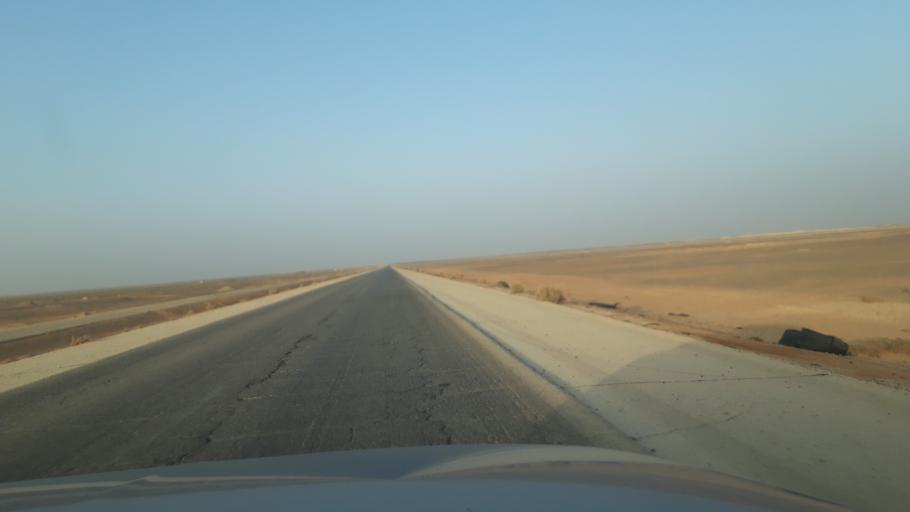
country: JO
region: Ma'an
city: Al Jafr
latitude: 30.2101
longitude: 36.0989
